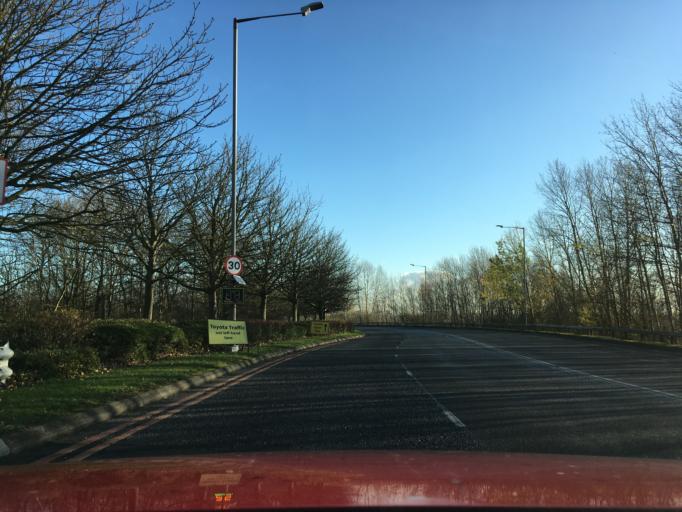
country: GB
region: England
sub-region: Derbyshire
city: Findern
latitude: 52.8693
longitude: -1.5672
